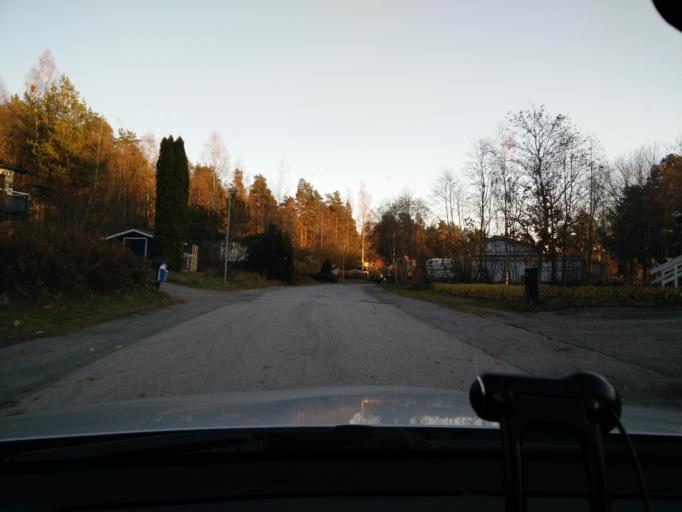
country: SE
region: Vaesternorrland
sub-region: Sundsvalls Kommun
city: Matfors
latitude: 62.3503
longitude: 17.0458
